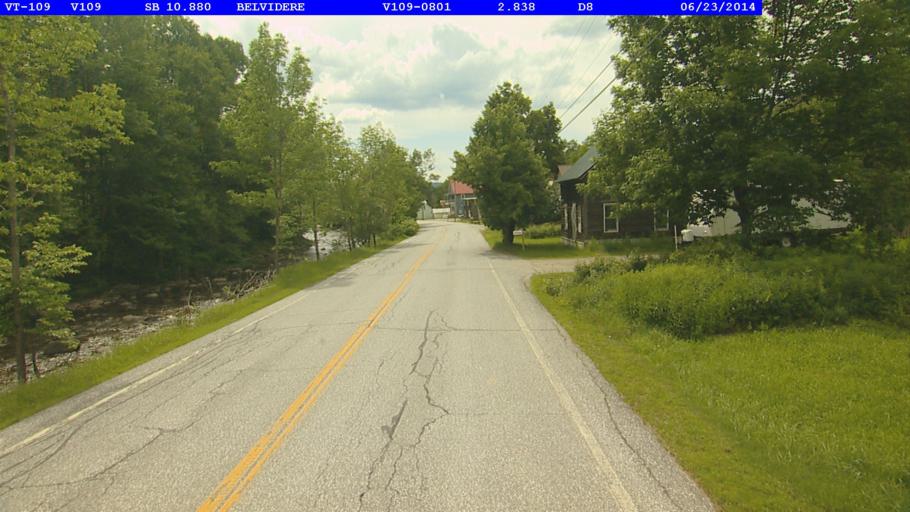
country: US
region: Vermont
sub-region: Lamoille County
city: Johnson
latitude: 44.7497
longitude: -72.6911
